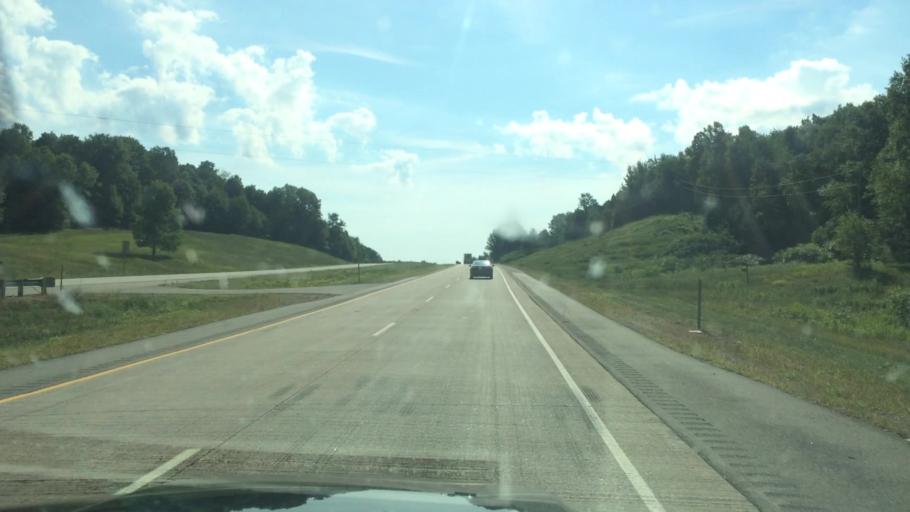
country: US
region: Wisconsin
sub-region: Shawano County
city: Wittenberg
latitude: 44.8036
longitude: -89.0163
